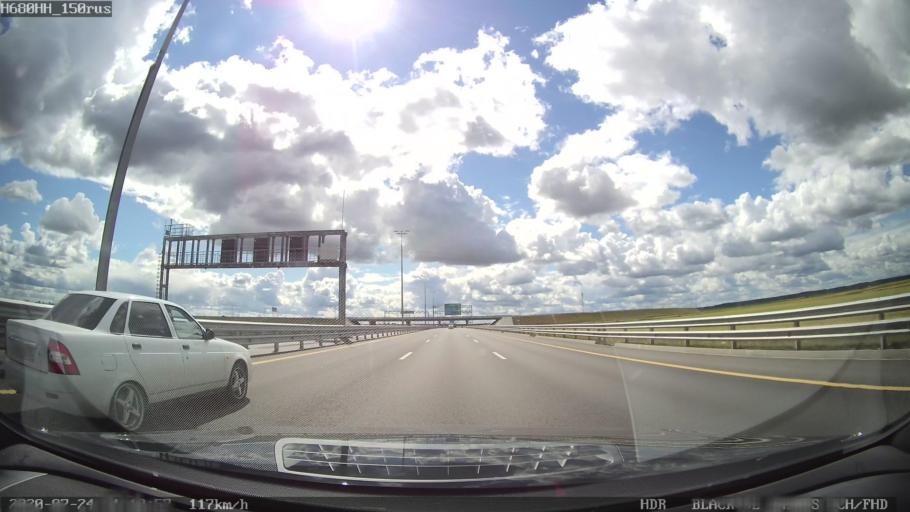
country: RU
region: St.-Petersburg
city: Tyarlevo
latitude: 59.7310
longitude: 30.5098
